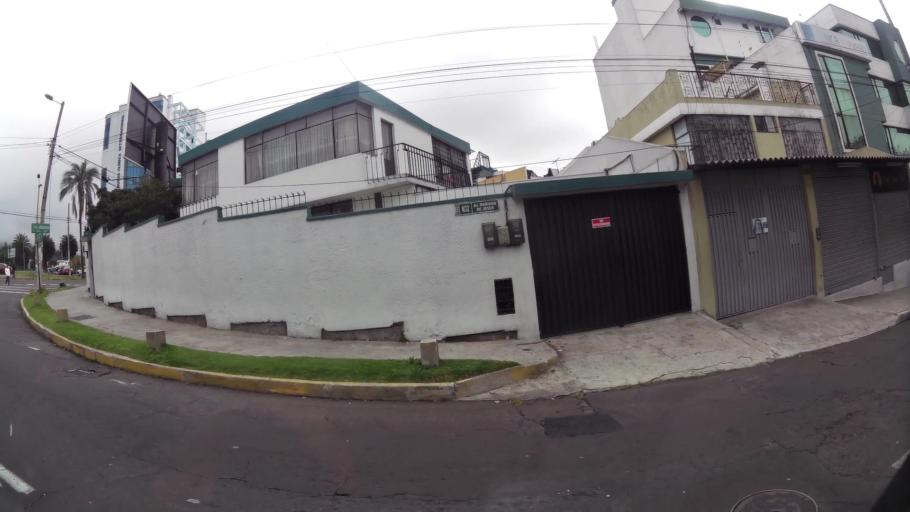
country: EC
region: Pichincha
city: Quito
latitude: -0.1867
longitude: -78.4949
